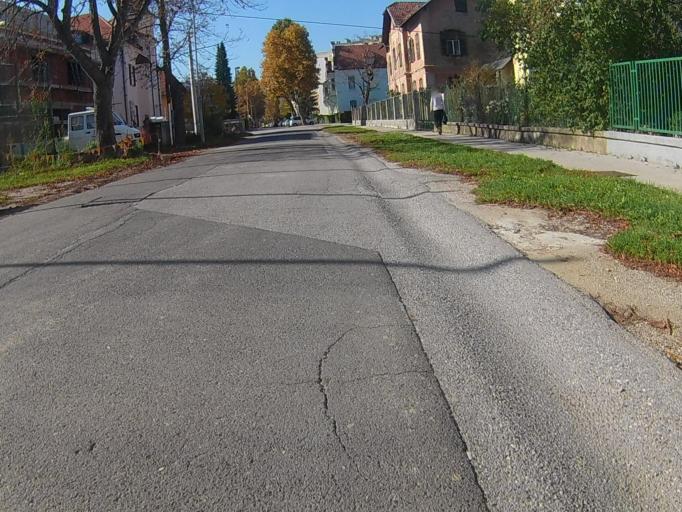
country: SI
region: Maribor
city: Maribor
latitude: 46.5654
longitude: 15.6395
